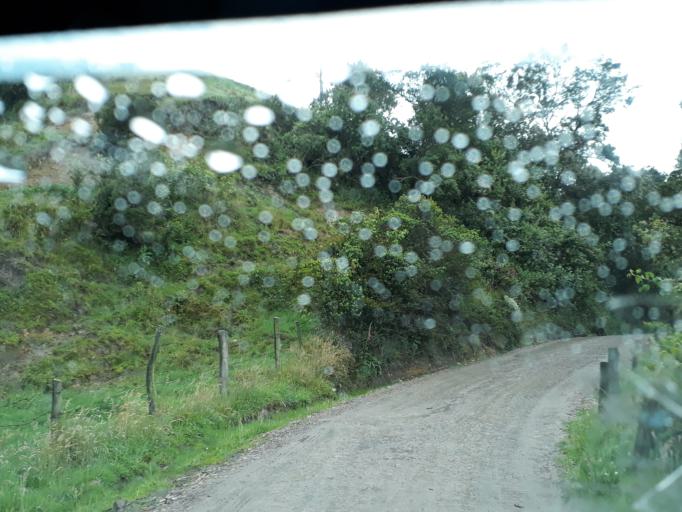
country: CO
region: Cundinamarca
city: La Mesa
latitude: 5.1671
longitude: -73.9122
